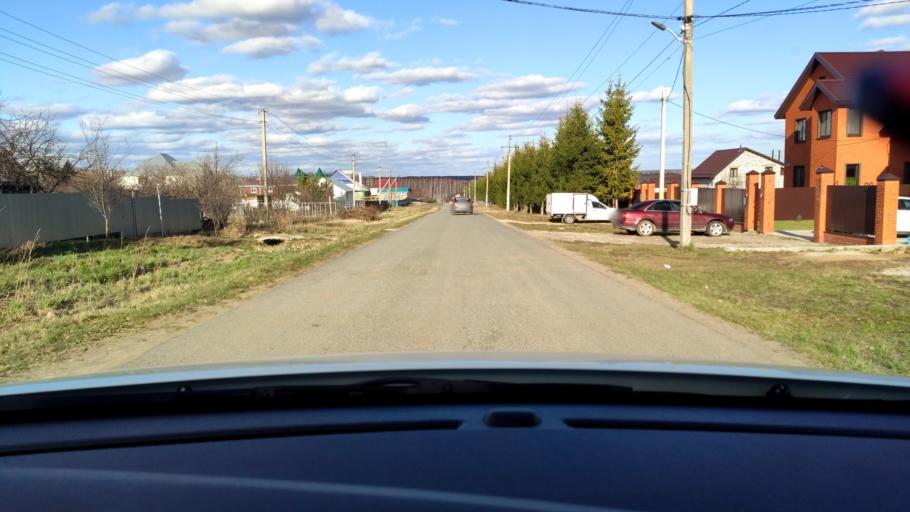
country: RU
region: Tatarstan
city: Vysokaya Gora
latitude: 55.8889
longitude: 49.3572
